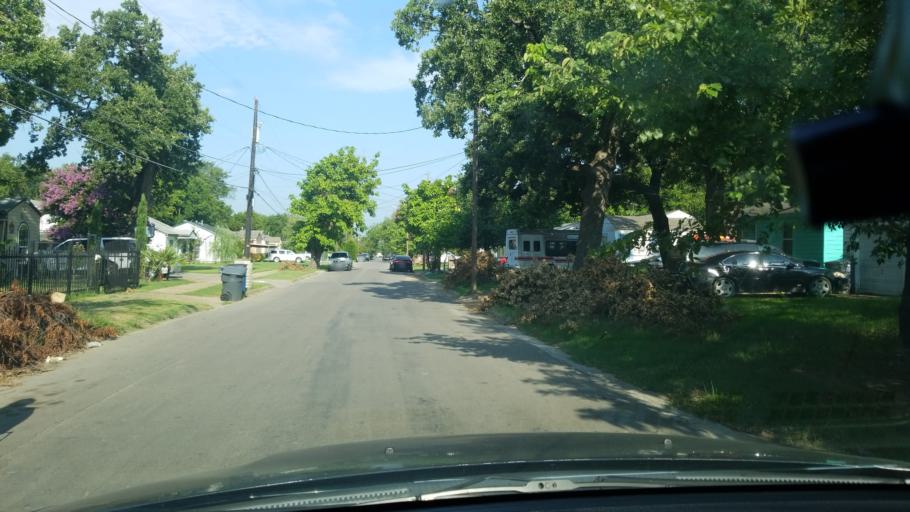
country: US
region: Texas
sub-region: Dallas County
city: Balch Springs
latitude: 32.7227
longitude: -96.6840
